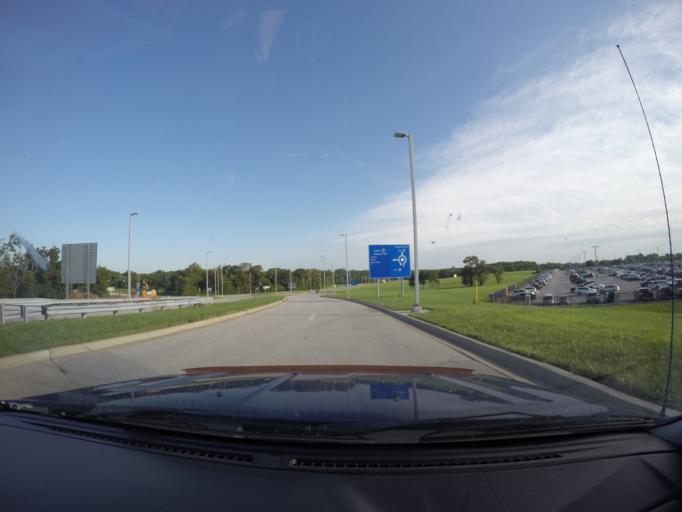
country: US
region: Missouri
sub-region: Platte County
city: Weatherby Lake
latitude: 39.3157
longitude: -94.6999
